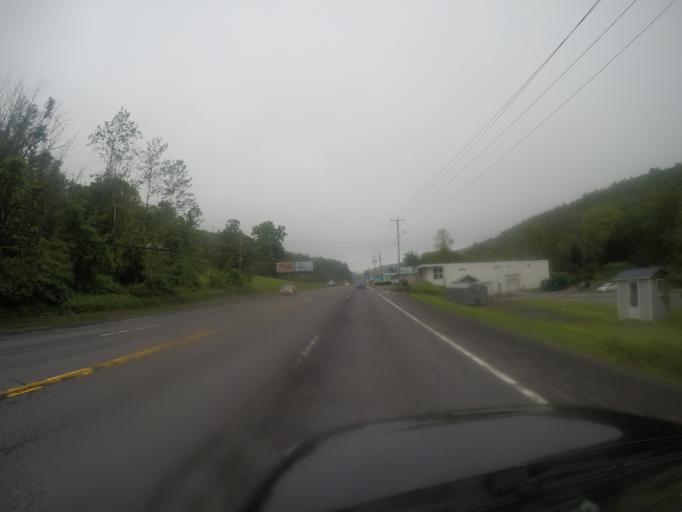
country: US
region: New York
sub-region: Ulster County
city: Hurley
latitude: 41.9597
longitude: -74.0555
